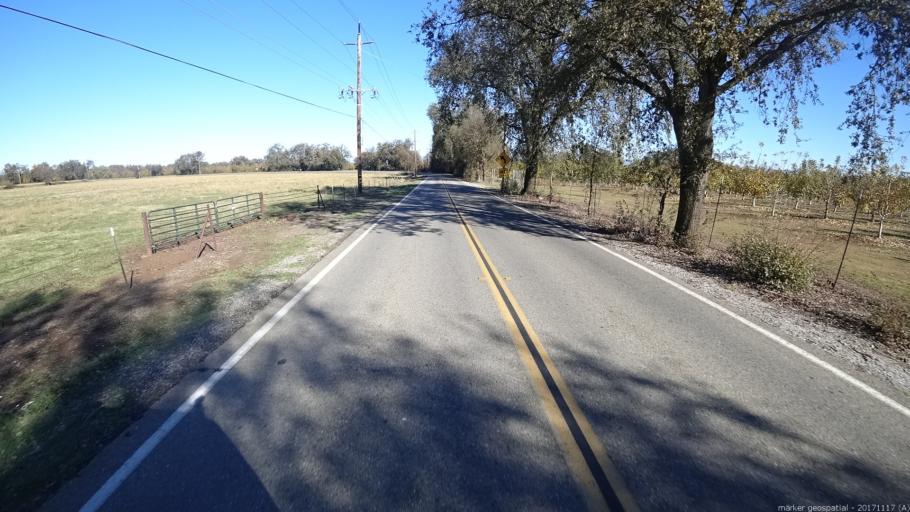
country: US
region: California
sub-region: Shasta County
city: Cottonwood
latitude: 40.4163
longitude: -122.2156
